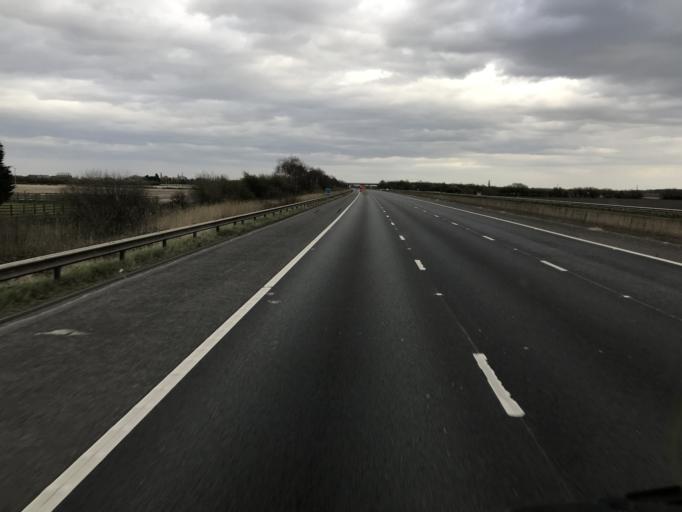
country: GB
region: England
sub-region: Doncaster
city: Hatfield
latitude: 53.5779
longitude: -0.9319
